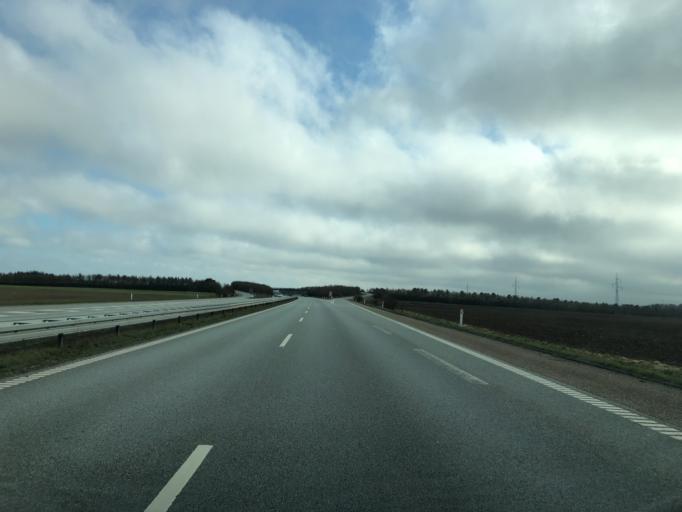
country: DK
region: North Denmark
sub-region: Hjorring Kommune
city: Hjorring
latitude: 57.4283
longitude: 10.0311
